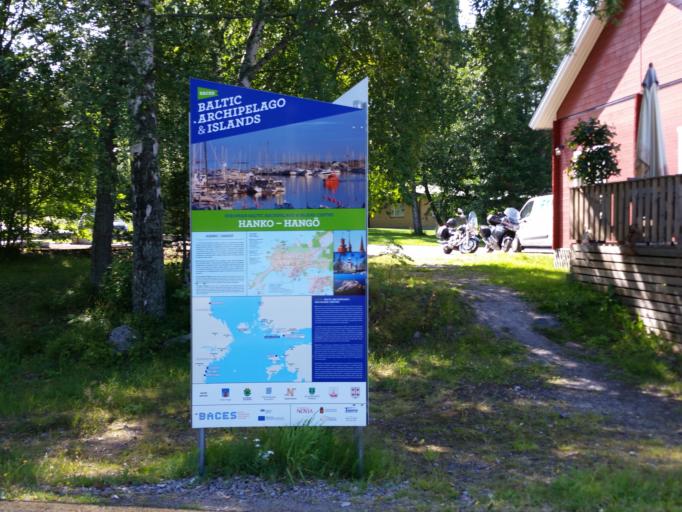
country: FI
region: Uusimaa
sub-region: Raaseporin
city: Hanko
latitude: 59.8419
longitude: 22.9482
